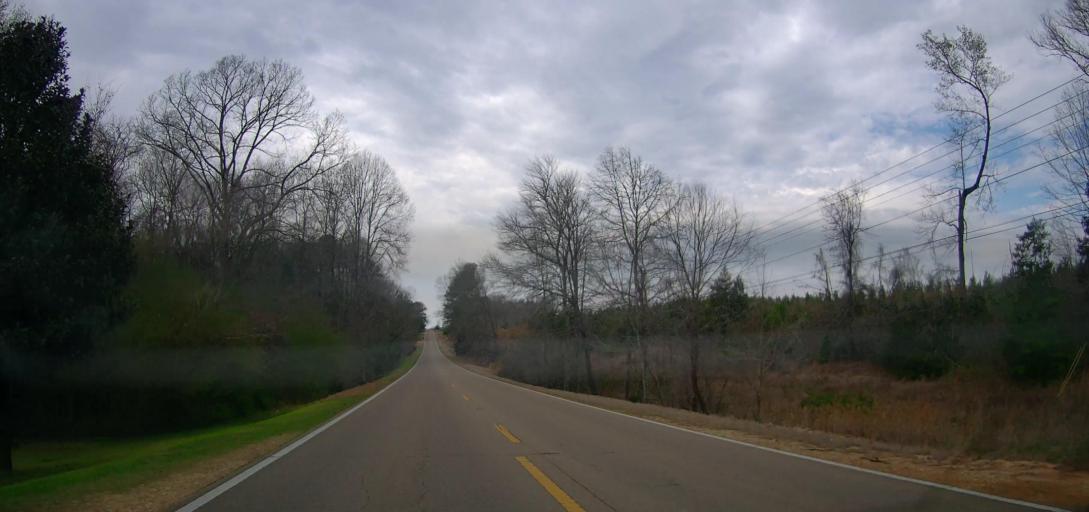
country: US
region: Mississippi
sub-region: Itawamba County
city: Fulton
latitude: 34.2753
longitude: -88.3514
